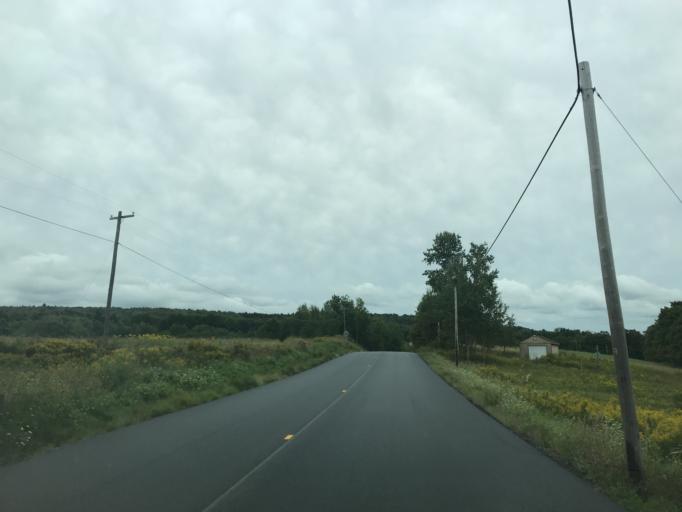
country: US
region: New York
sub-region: Delaware County
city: Stamford
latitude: 42.5265
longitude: -74.6214
